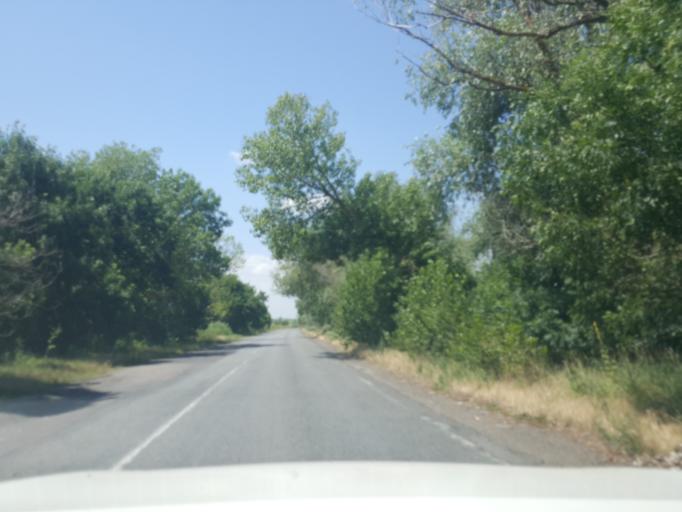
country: UA
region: Odessa
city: Bilyayivka
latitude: 46.4102
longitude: 30.1378
